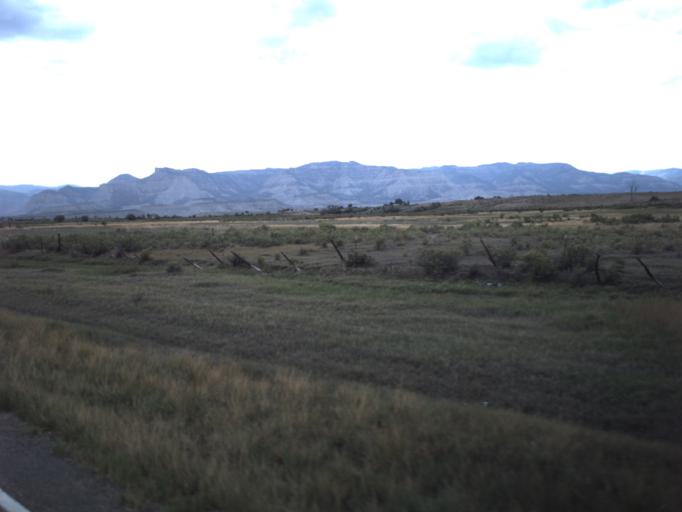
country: US
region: Utah
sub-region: Emery County
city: Huntington
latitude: 39.3451
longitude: -110.8968
